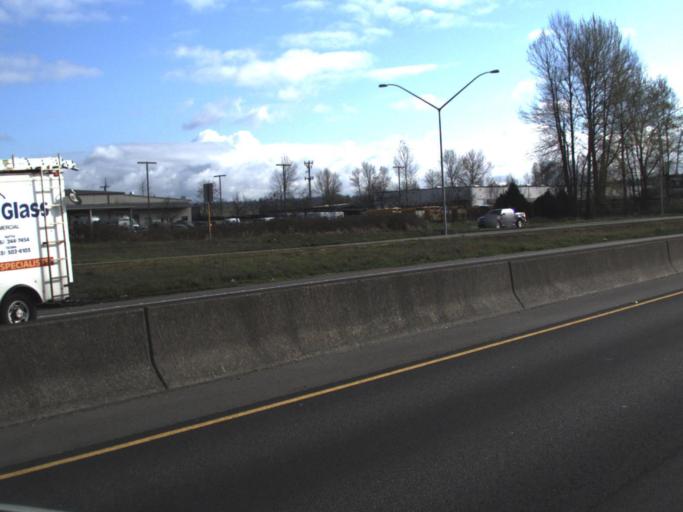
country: US
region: Washington
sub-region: King County
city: Auburn
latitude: 47.3023
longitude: -122.2500
